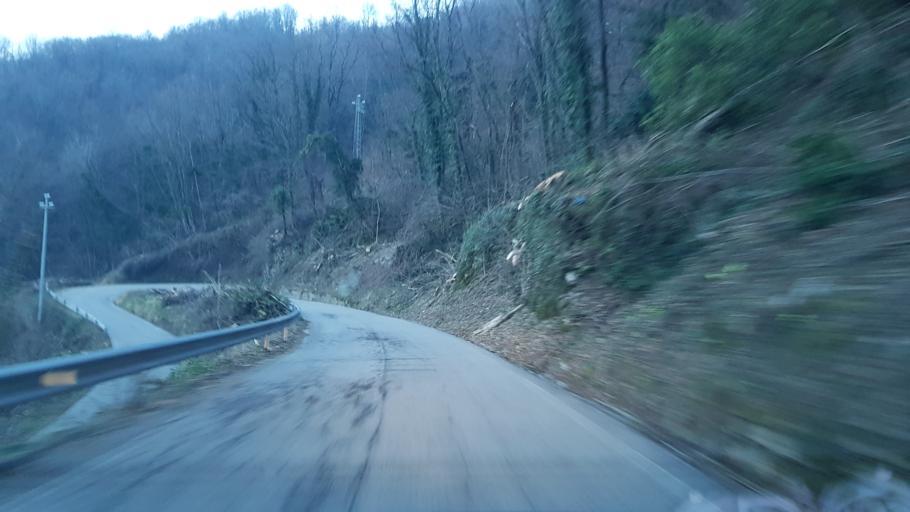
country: IT
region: Friuli Venezia Giulia
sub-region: Provincia di Udine
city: Attimis
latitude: 46.1955
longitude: 13.3360
